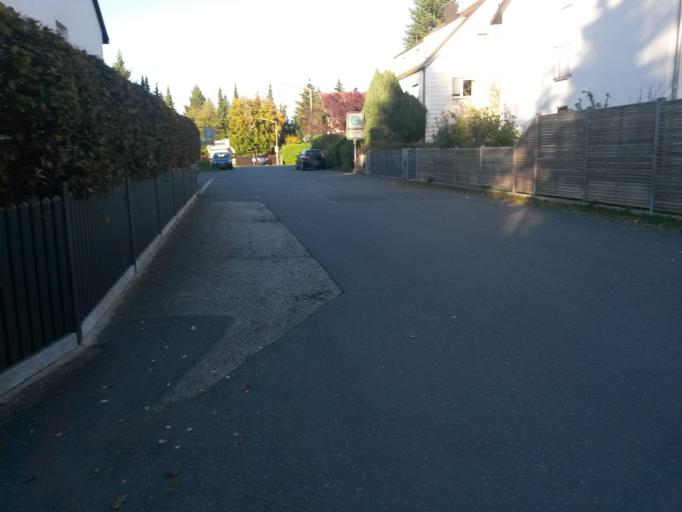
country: DE
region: Bavaria
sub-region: Regierungsbezirk Mittelfranken
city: Zirndorf
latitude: 49.4490
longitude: 10.9695
